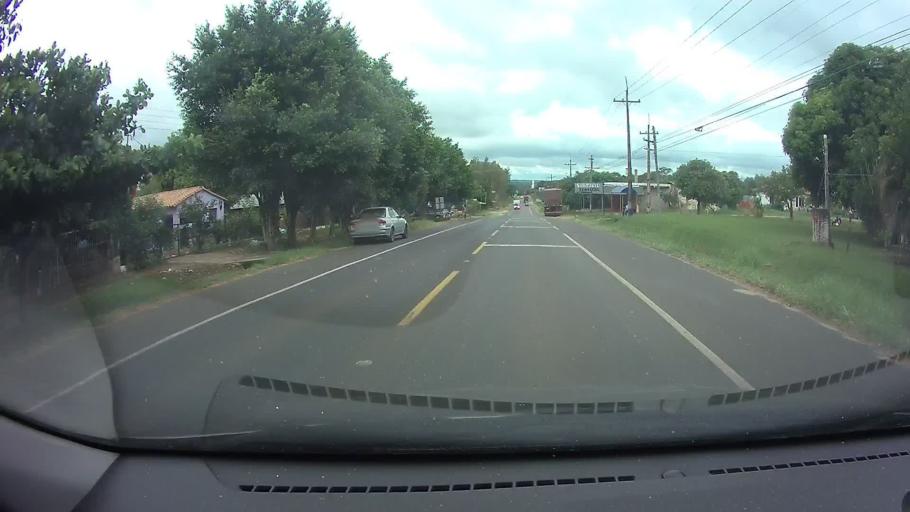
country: PY
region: Central
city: Guarambare
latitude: -25.5012
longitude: -57.4933
